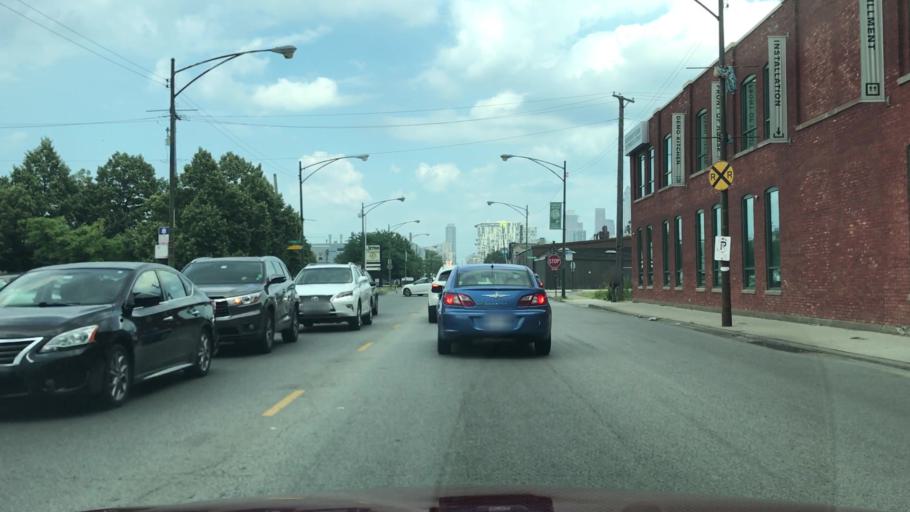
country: US
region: Illinois
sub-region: Cook County
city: Chicago
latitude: 41.9035
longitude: -87.6550
